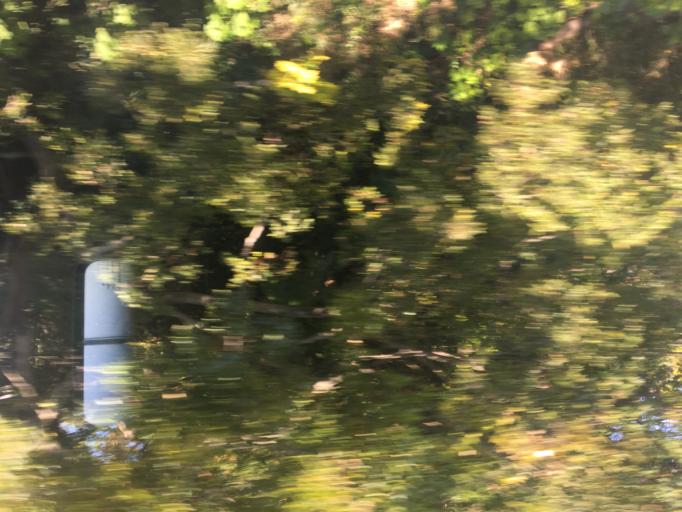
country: JP
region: Tochigi
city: Ashikaga
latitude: 36.3356
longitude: 139.4323
